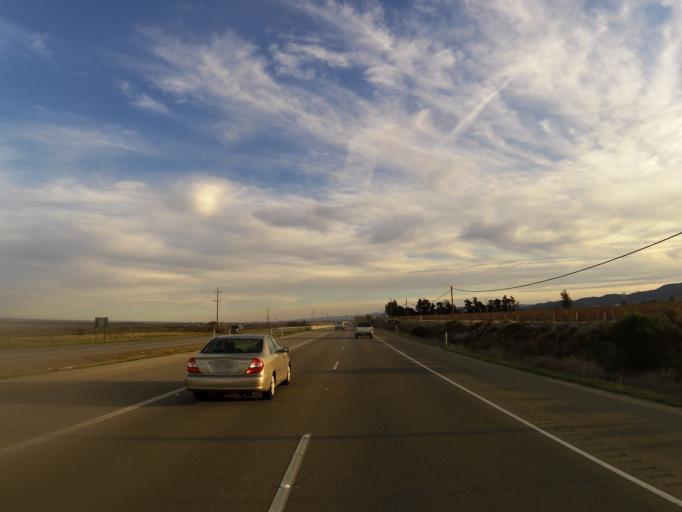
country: US
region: California
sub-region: Monterey County
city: Greenfield
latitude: 36.2753
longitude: -121.1851
